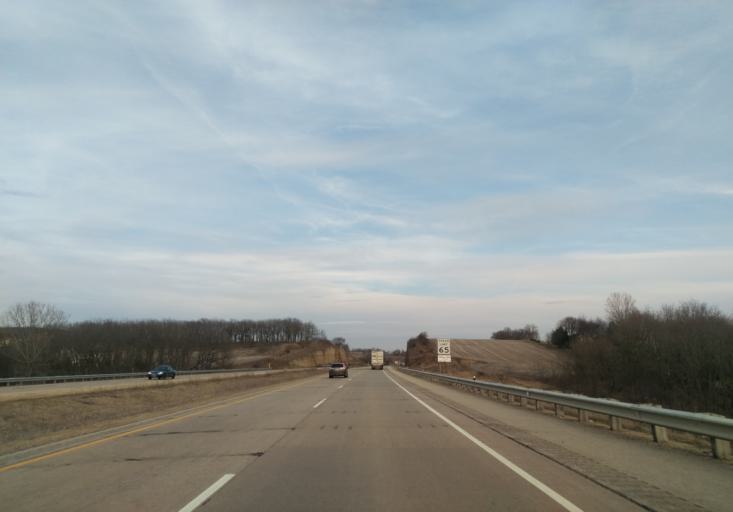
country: US
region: Wisconsin
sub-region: Iowa County
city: Barneveld
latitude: 43.0104
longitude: -89.8895
